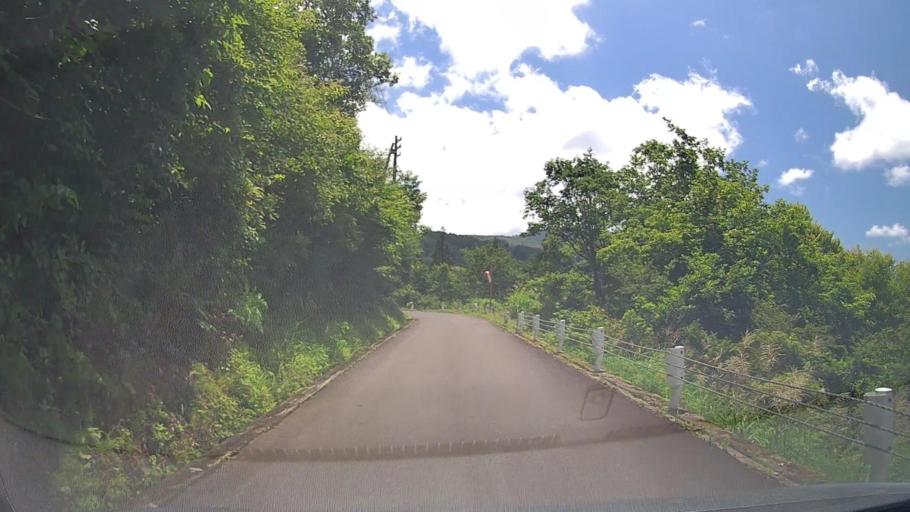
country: JP
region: Nagano
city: Iiyama
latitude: 36.9345
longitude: 138.4645
